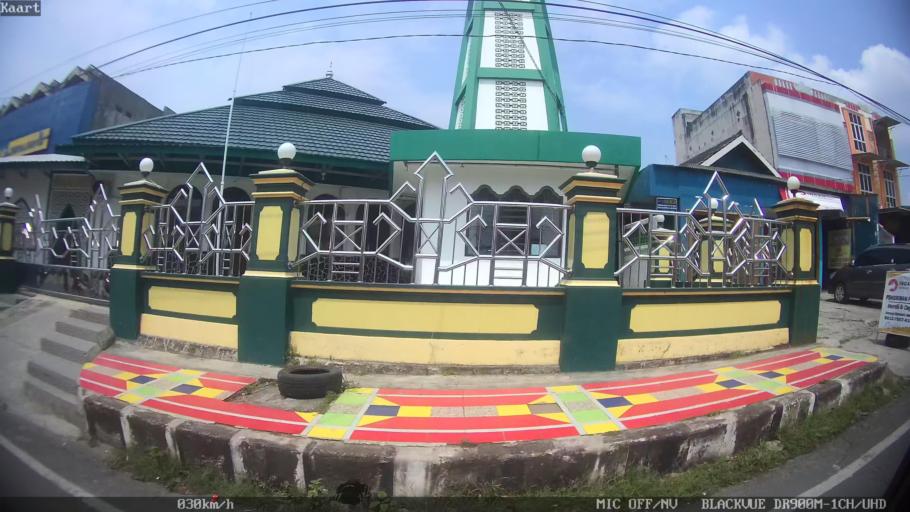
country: ID
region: Lampung
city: Bandarlampung
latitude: -5.4352
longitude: 105.2626
